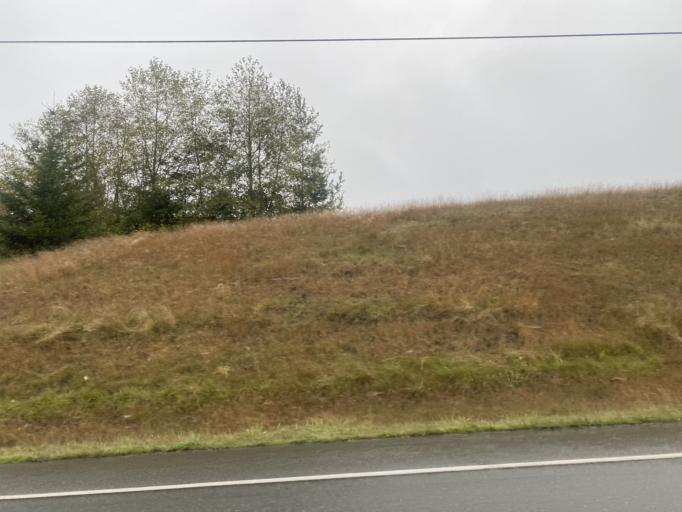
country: US
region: Washington
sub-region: Island County
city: Freeland
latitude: 48.0329
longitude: -122.5069
